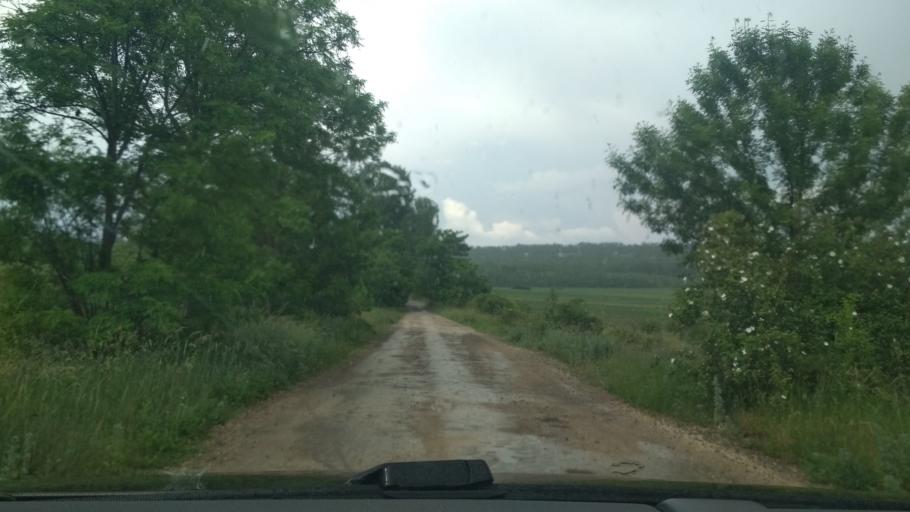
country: MD
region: Singerei
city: Biruinta
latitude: 47.7435
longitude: 28.1375
